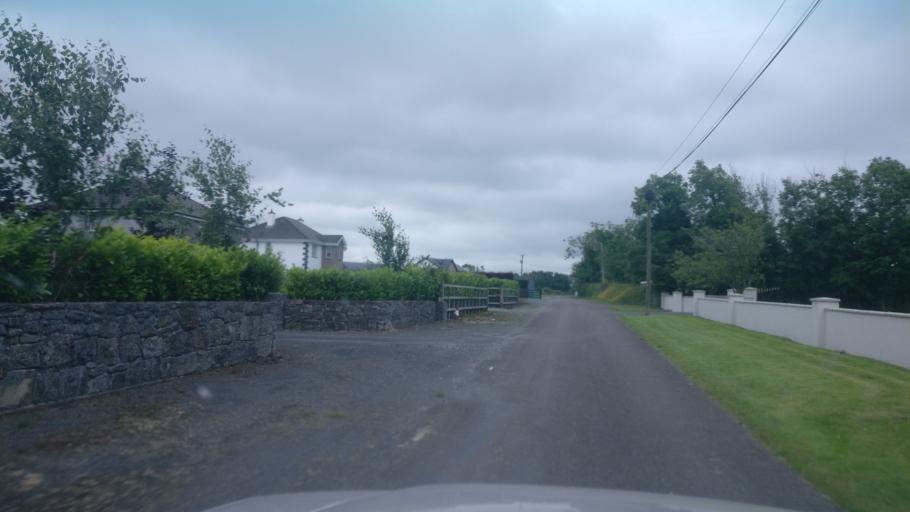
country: IE
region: Connaught
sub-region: County Galway
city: Ballinasloe
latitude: 53.2968
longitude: -8.3423
